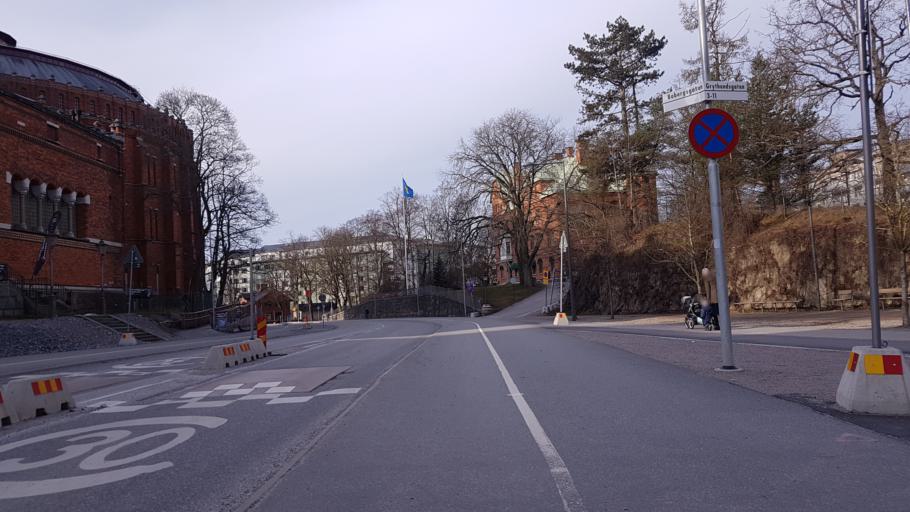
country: SE
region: Stockholm
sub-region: Stockholms Kommun
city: OEstermalm
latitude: 59.3582
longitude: 18.0905
